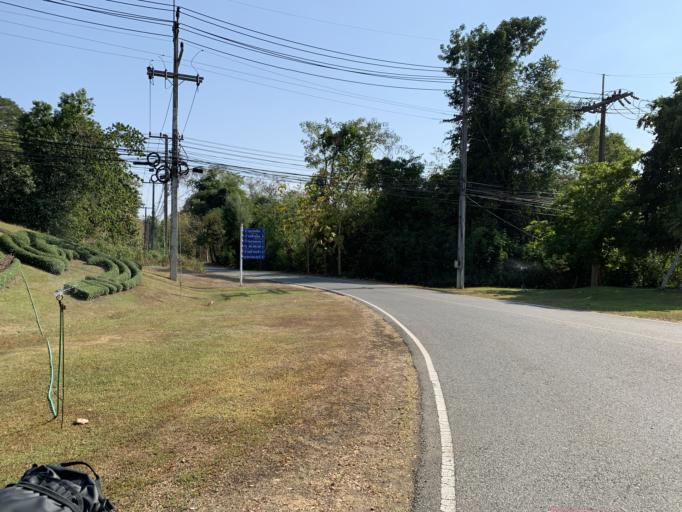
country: TH
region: Uttaradit
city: Nam Pat
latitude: 17.7400
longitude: 100.5567
